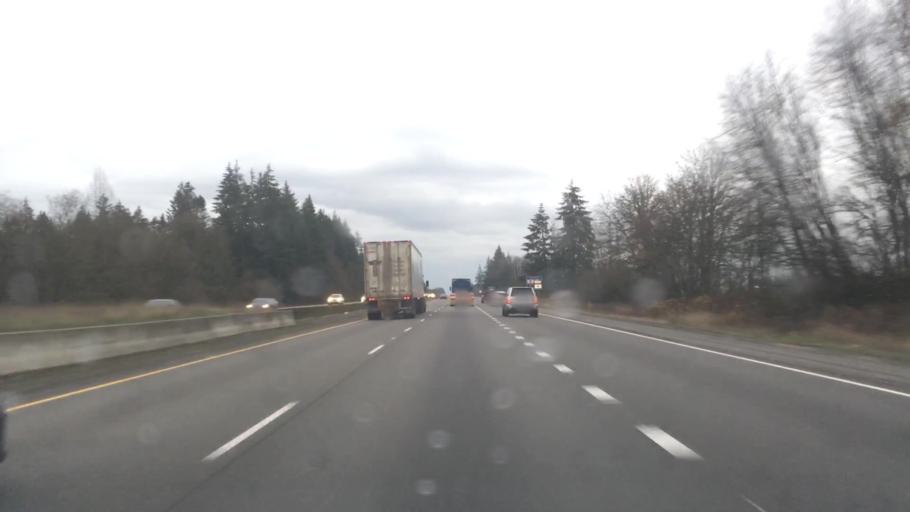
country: US
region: Washington
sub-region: Lewis County
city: Napavine
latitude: 46.5614
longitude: -122.8768
